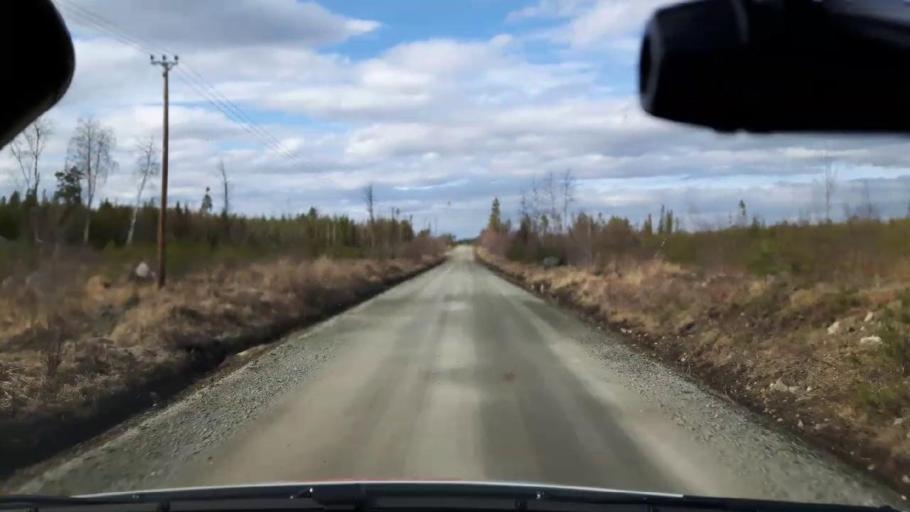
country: SE
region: Jaemtland
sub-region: Bergs Kommun
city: Hoverberg
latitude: 62.8369
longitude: 14.6662
